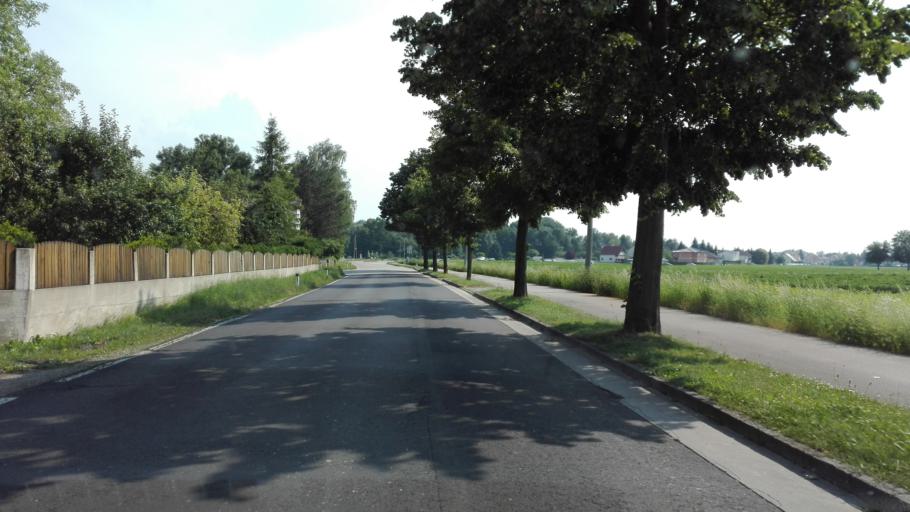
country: AT
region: Upper Austria
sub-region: Politischer Bezirk Linz-Land
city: Traun
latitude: 48.2318
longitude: 14.2656
